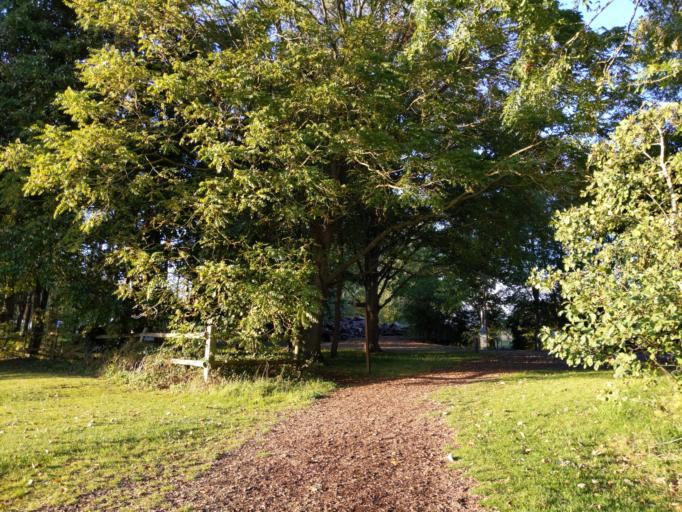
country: GB
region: England
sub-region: Oxfordshire
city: Radley
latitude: 51.6951
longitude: -1.2458
